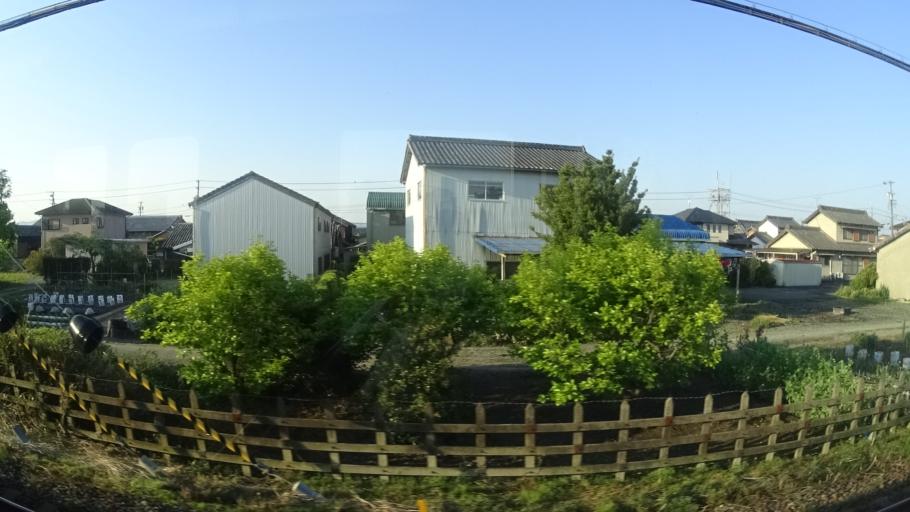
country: JP
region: Mie
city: Ise
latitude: 34.5375
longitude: 136.6203
